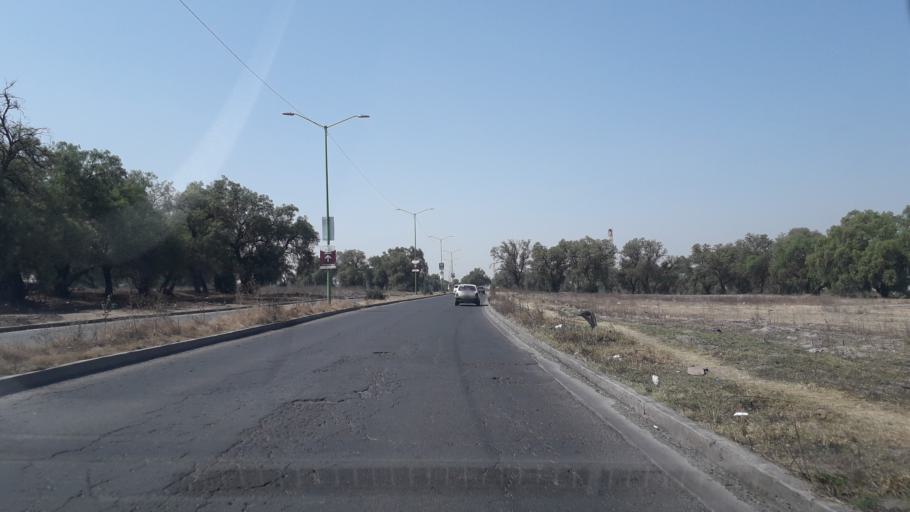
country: MX
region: Mexico
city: Santo Tomas Chiconautla
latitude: 19.6592
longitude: -99.0124
